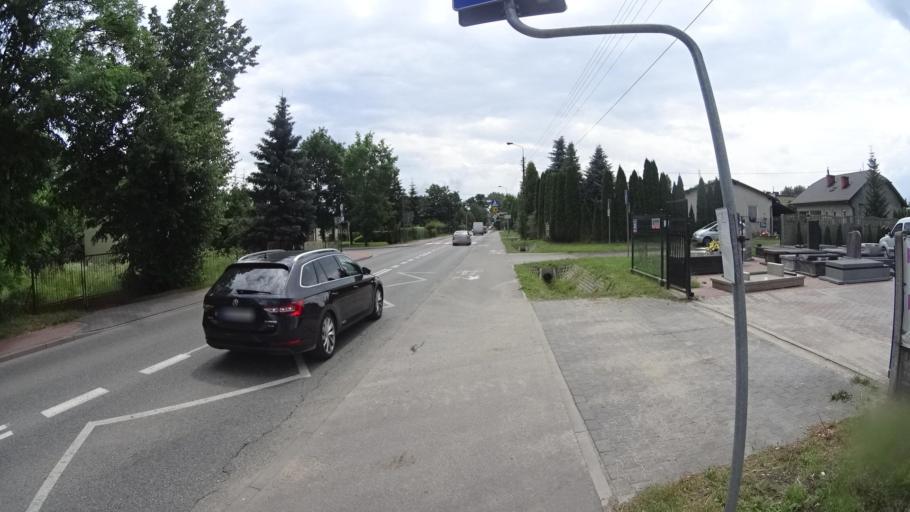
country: PL
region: Masovian Voivodeship
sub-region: Powiat pruszkowski
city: Nadarzyn
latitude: 52.0983
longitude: 20.8062
